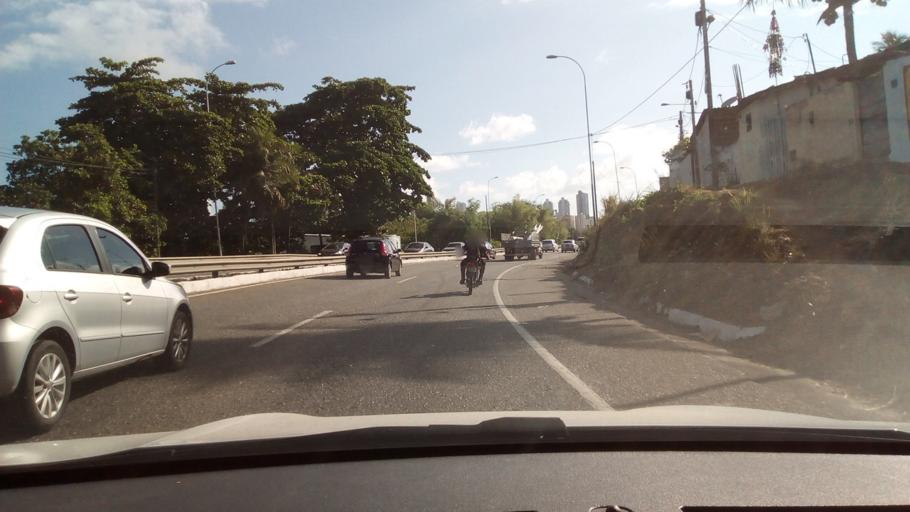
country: BR
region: Paraiba
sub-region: Joao Pessoa
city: Joao Pessoa
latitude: -7.1291
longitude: -34.8497
